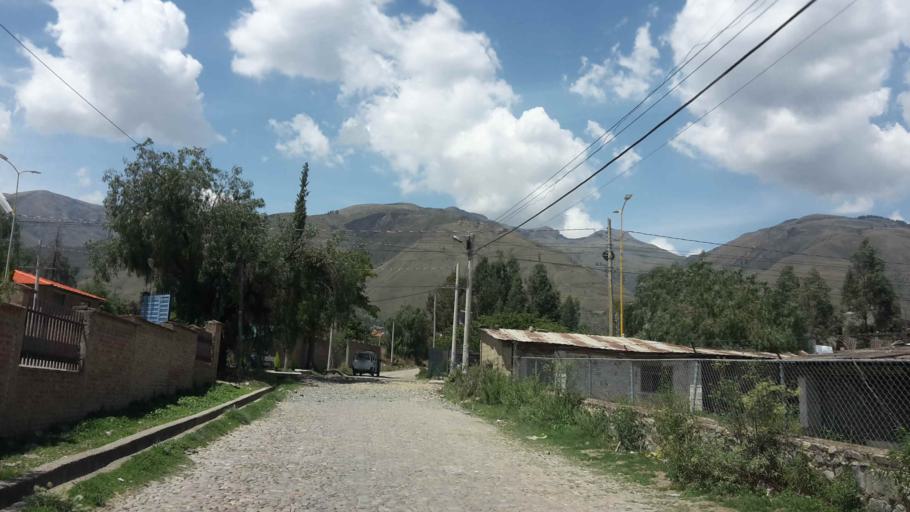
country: BO
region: Cochabamba
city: Cochabamba
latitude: -17.3448
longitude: -66.2000
